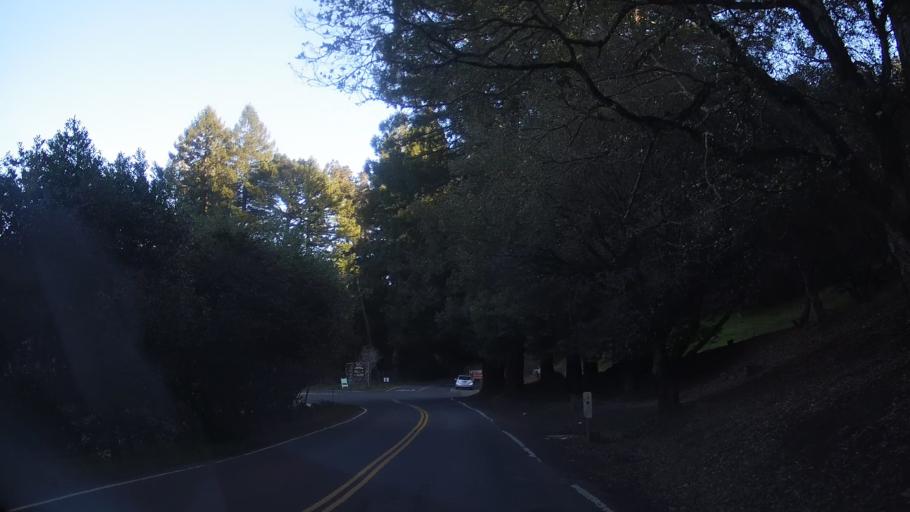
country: US
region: California
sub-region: Alameda County
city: Berkeley
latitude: 37.8913
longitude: -122.2500
